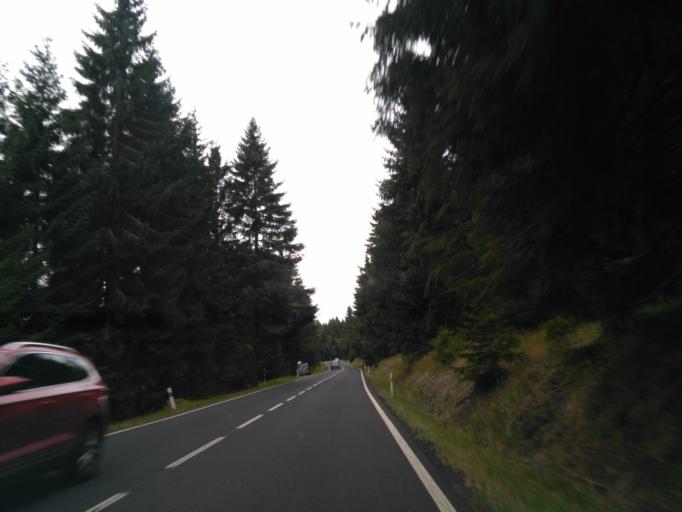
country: CZ
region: Karlovarsky
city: Merklin
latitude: 50.3777
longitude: 12.8742
